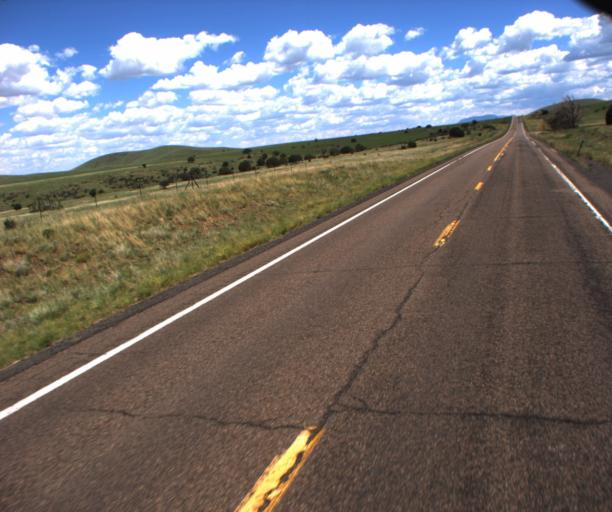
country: US
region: Arizona
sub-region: Apache County
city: Springerville
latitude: 34.2310
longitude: -109.4947
